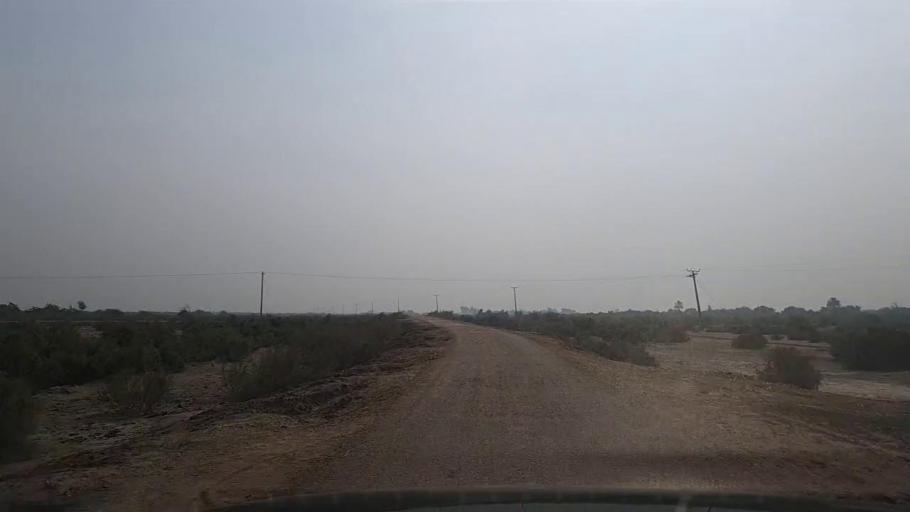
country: PK
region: Sindh
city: Mirpur Sakro
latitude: 24.3970
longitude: 67.7513
